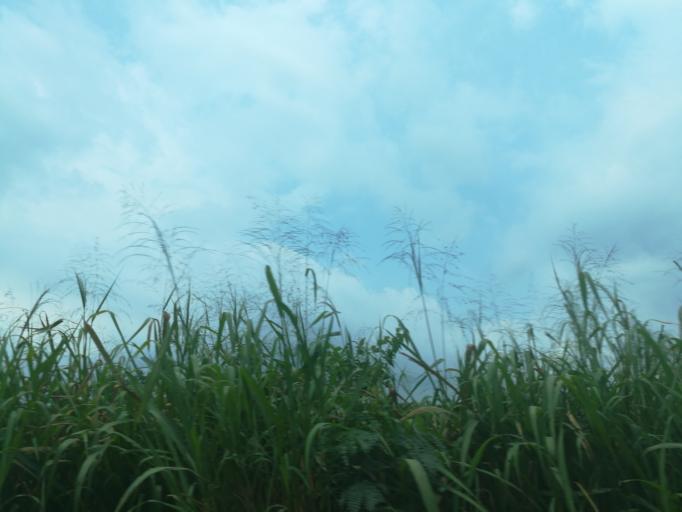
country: NG
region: Lagos
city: Ikorodu
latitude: 6.6735
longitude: 3.6567
